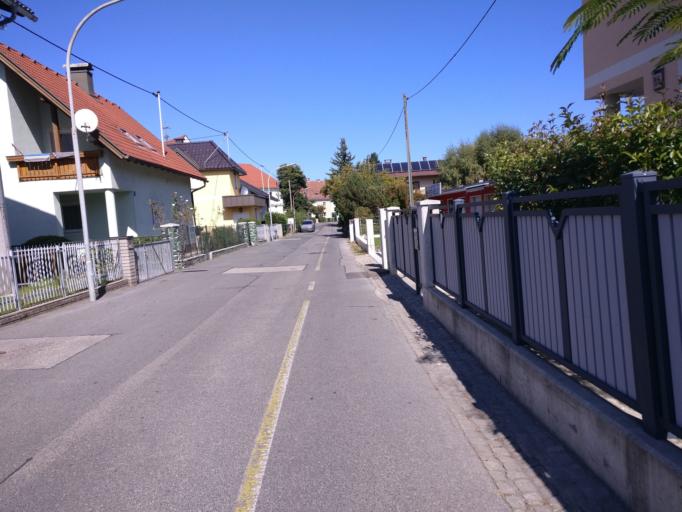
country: AT
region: Carinthia
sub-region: Klagenfurt am Woerthersee
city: Klagenfurt am Woerthersee
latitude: 46.6113
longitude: 14.2837
